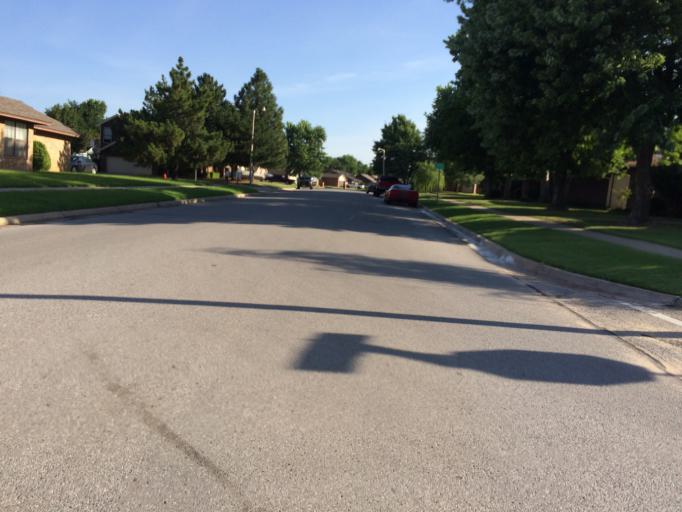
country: US
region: Oklahoma
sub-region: Cleveland County
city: Norman
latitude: 35.2208
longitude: -97.5044
